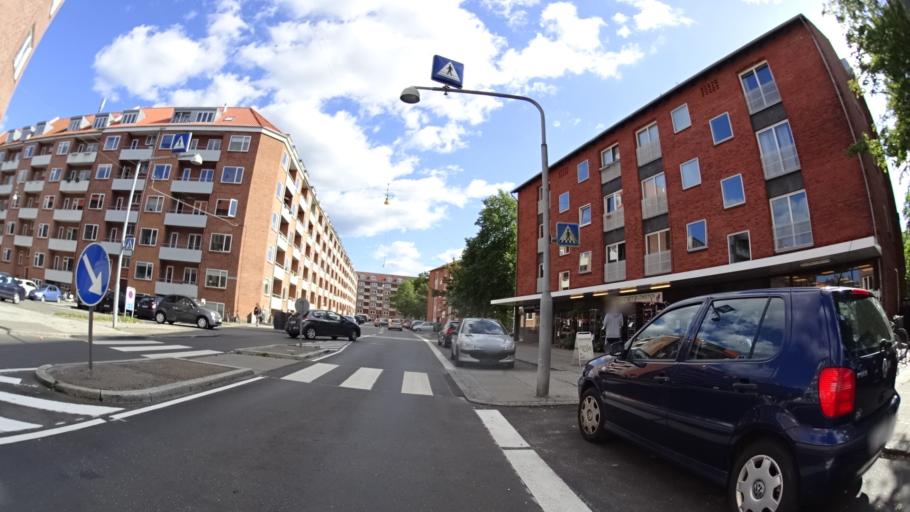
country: DK
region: Central Jutland
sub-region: Arhus Kommune
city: Arhus
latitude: 56.1451
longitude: 10.1857
